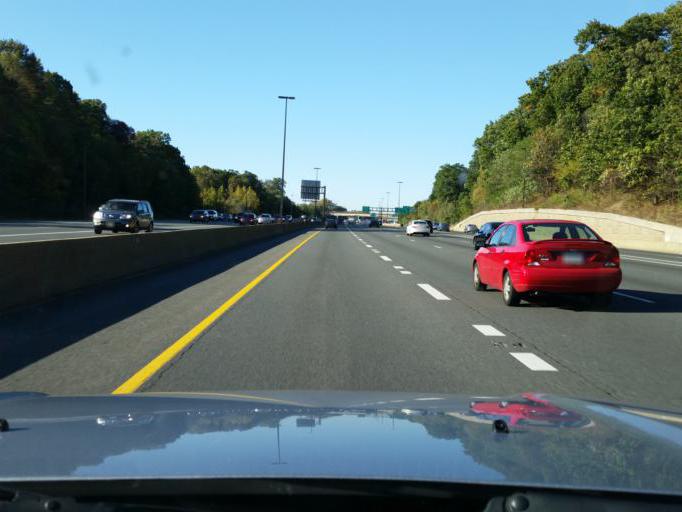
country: US
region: Maryland
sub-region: Montgomery County
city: North Bethesda
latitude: 39.0501
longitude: -77.1518
